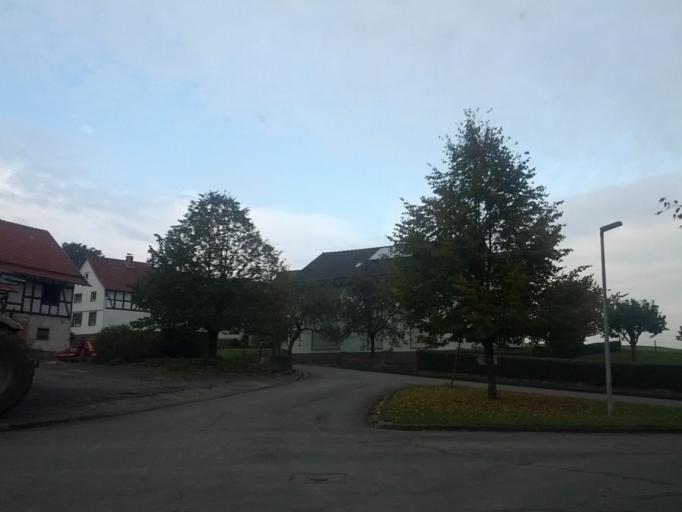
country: DE
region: Hesse
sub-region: Regierungsbezirk Kassel
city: Herleshausen
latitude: 51.0412
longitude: 10.1482
